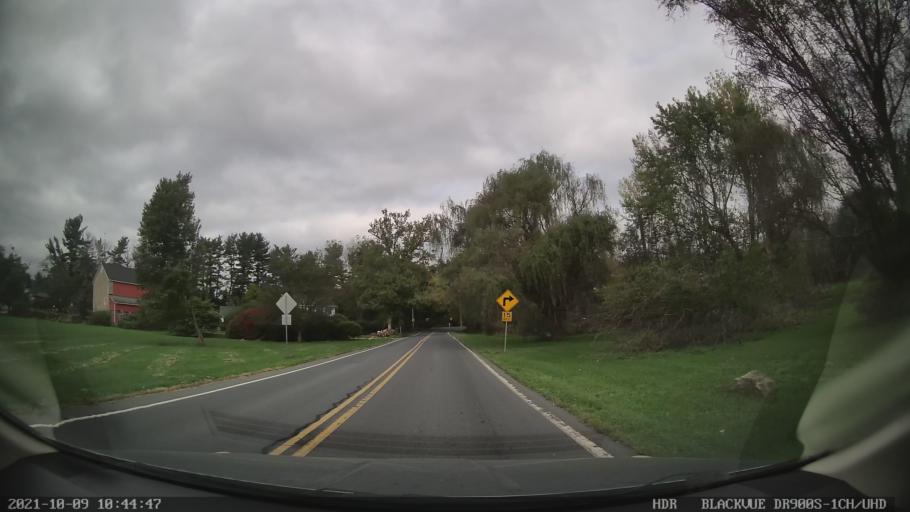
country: US
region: Pennsylvania
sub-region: Lehigh County
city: Ancient Oaks
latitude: 40.5395
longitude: -75.5922
